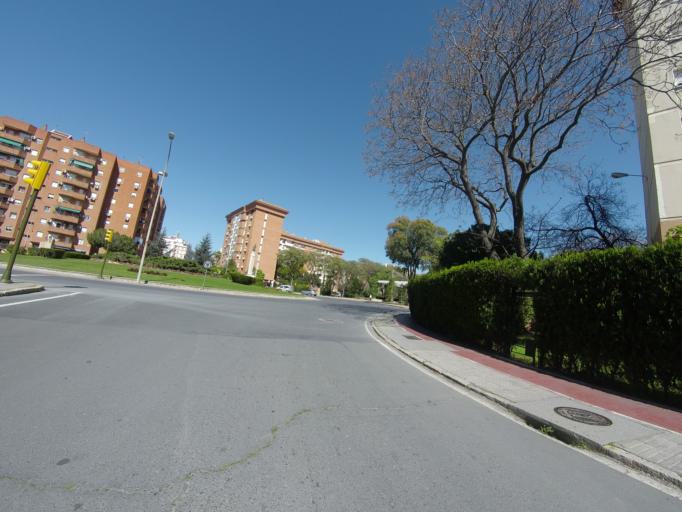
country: ES
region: Andalusia
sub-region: Provincia de Huelva
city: Huelva
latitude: 37.2636
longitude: -6.9402
